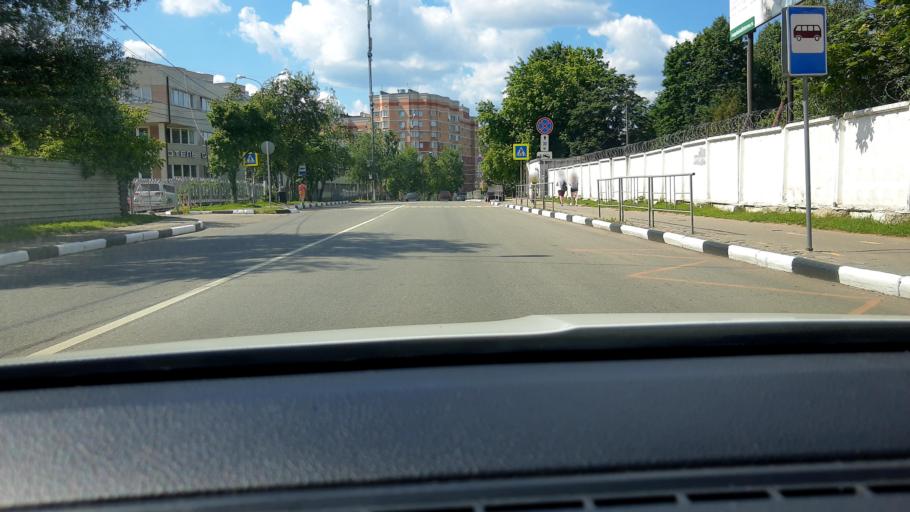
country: RU
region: Moskovskaya
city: Odintsovo
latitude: 55.6872
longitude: 37.2585
